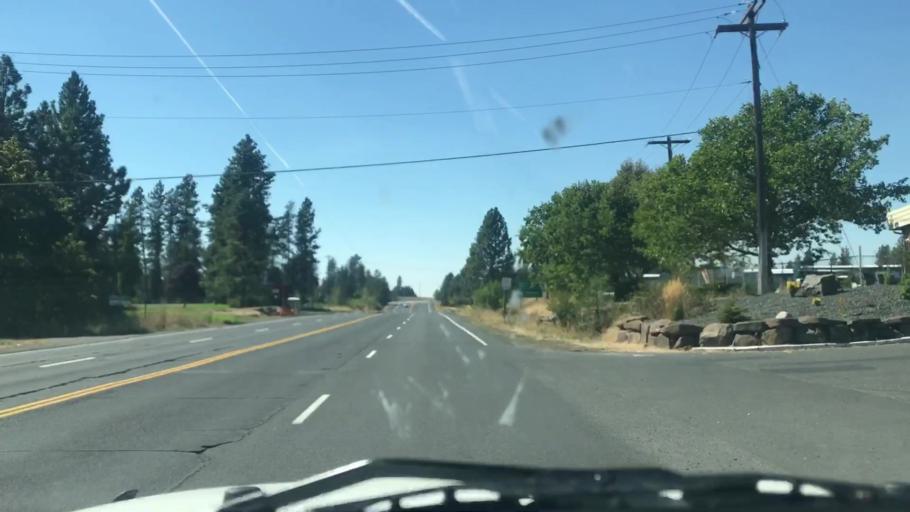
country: US
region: Washington
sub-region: Spokane County
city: Spokane
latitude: 47.6431
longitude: -117.4912
